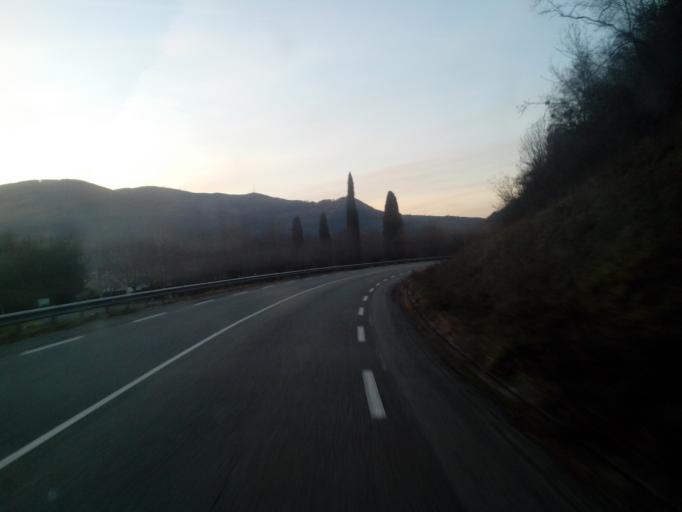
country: FR
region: Midi-Pyrenees
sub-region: Departement de l'Ariege
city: Saint-Paul-de-Jarrat
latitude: 42.9159
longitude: 1.6592
